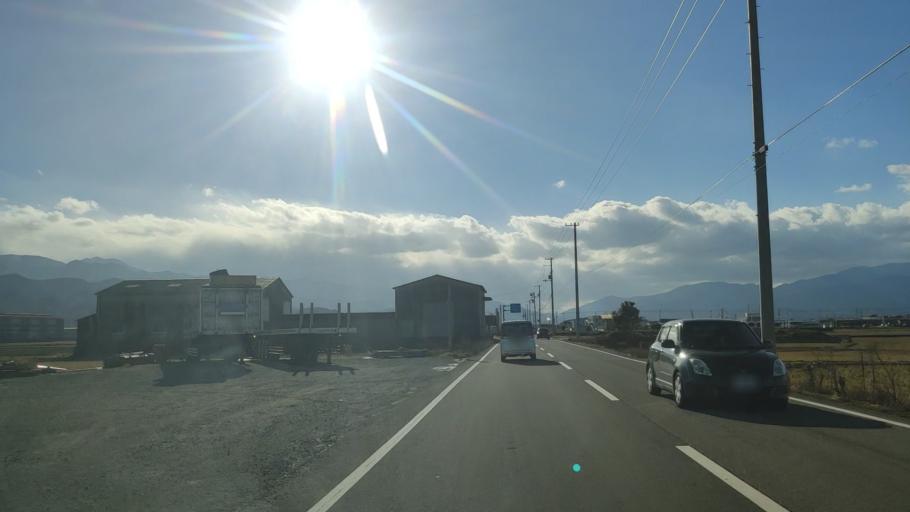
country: JP
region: Ehime
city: Saijo
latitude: 33.9130
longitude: 133.1153
